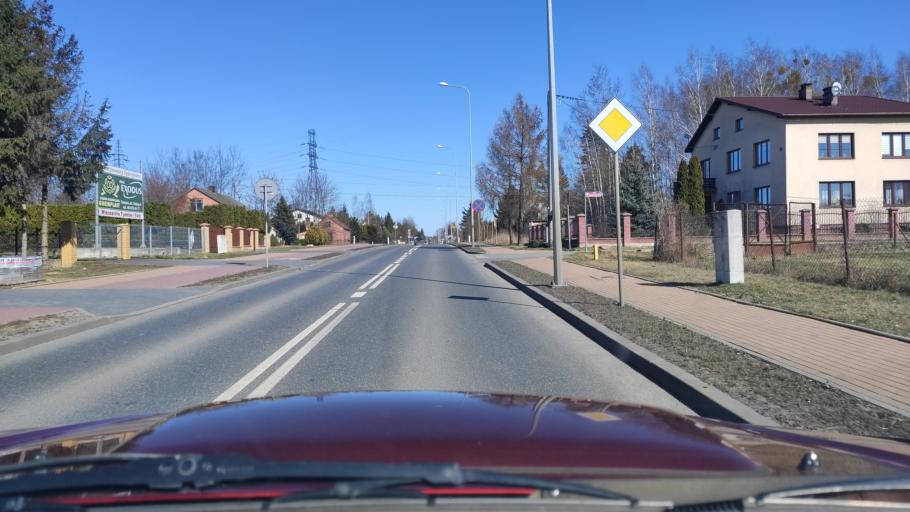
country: PL
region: Masovian Voivodeship
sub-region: Powiat zwolenski
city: Zwolen
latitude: 51.3671
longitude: 21.5851
